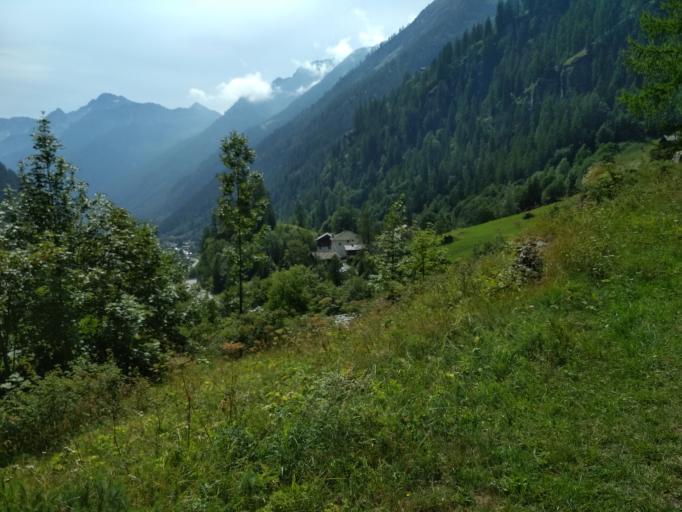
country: IT
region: Aosta Valley
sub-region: Valle d'Aosta
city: Gressoney-La-Trinite
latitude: 45.8090
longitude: 7.8249
